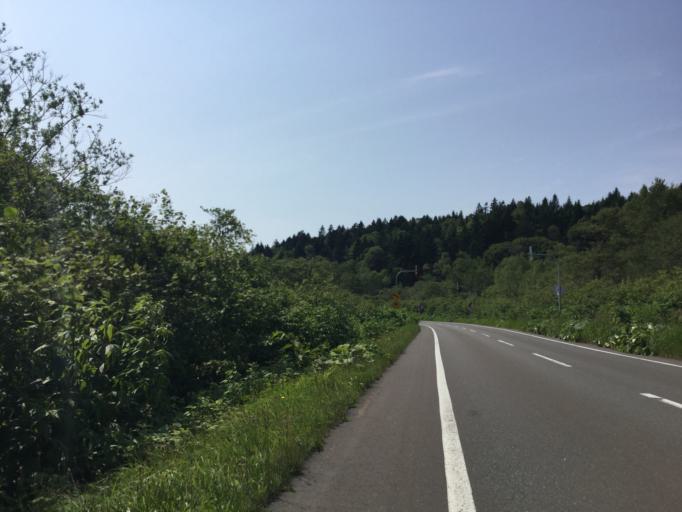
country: JP
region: Hokkaido
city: Makubetsu
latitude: 45.4102
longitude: 142.0022
